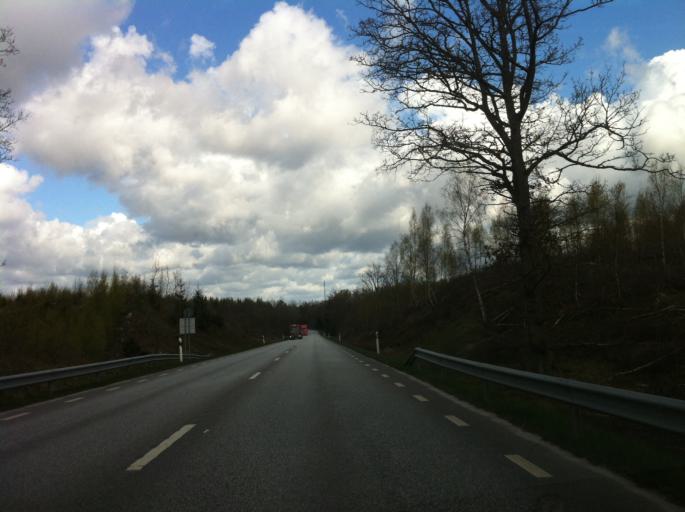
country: SE
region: Skane
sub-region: Horby Kommun
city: Hoerby
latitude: 55.8930
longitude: 13.6239
